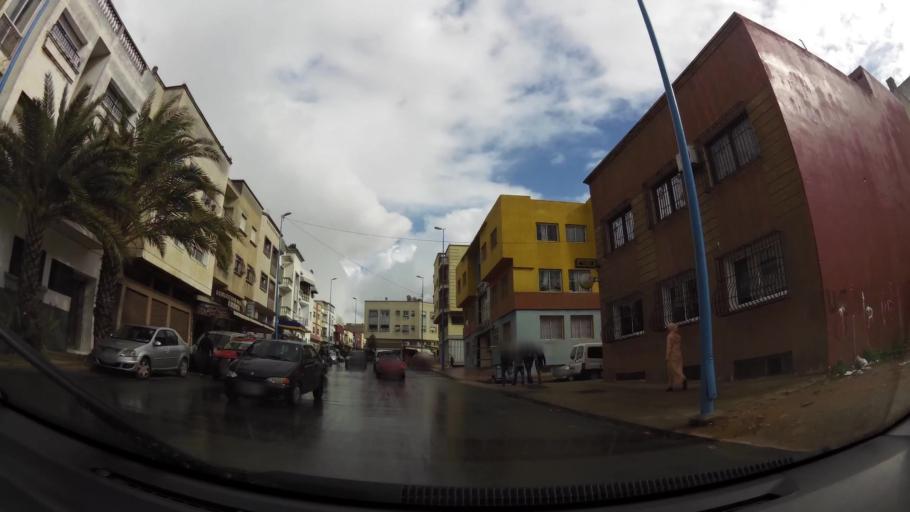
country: MA
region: Grand Casablanca
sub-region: Casablanca
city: Casablanca
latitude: 33.5652
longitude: -7.6943
